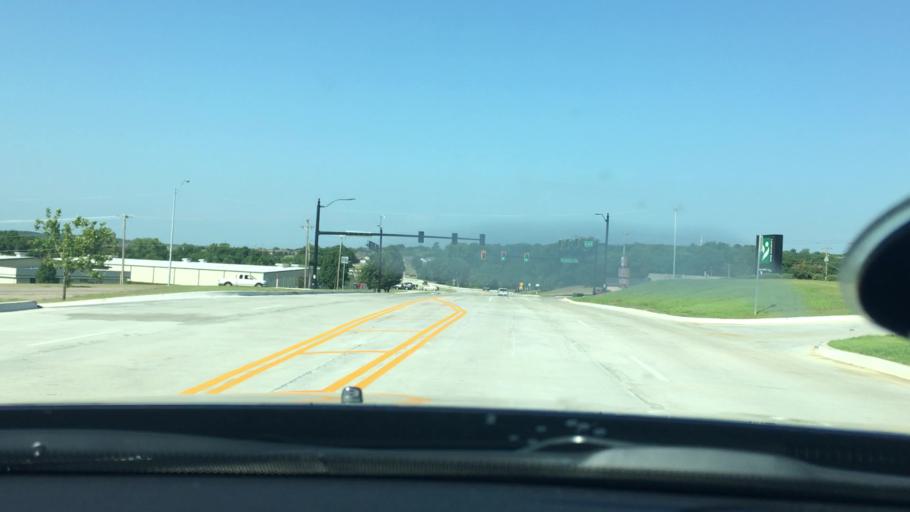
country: US
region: Oklahoma
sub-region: Pontotoc County
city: Ada
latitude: 34.7628
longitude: -96.6629
